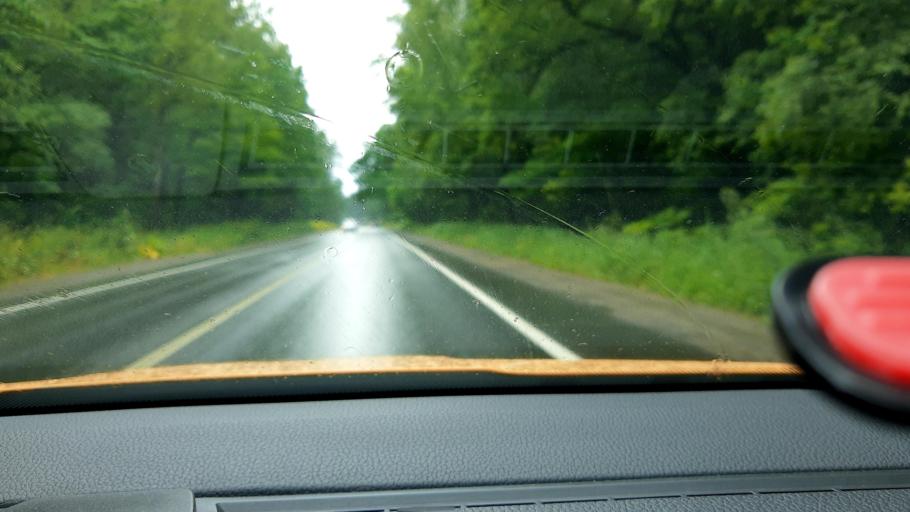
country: RU
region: Moskovskaya
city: Pirogovskiy
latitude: 55.9990
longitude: 37.6895
